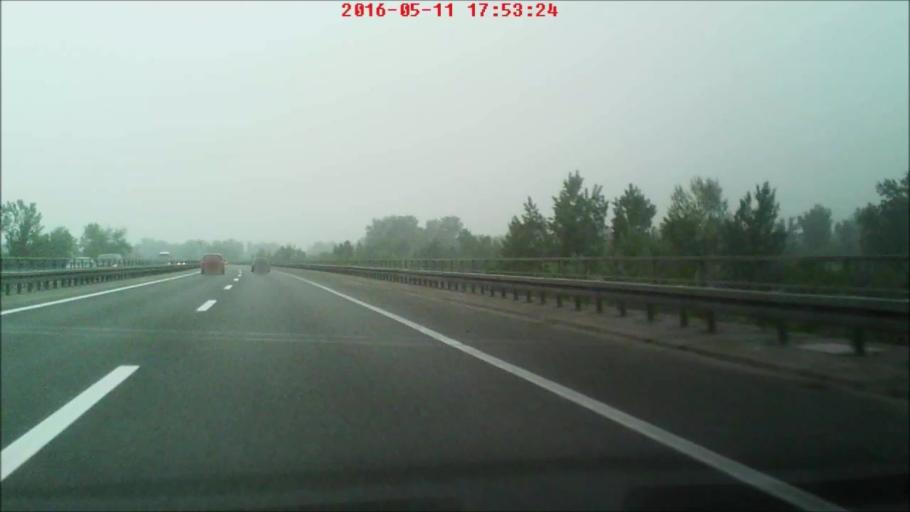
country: HR
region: Zagrebacka
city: Zapresic
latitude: 45.8342
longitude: 15.8187
